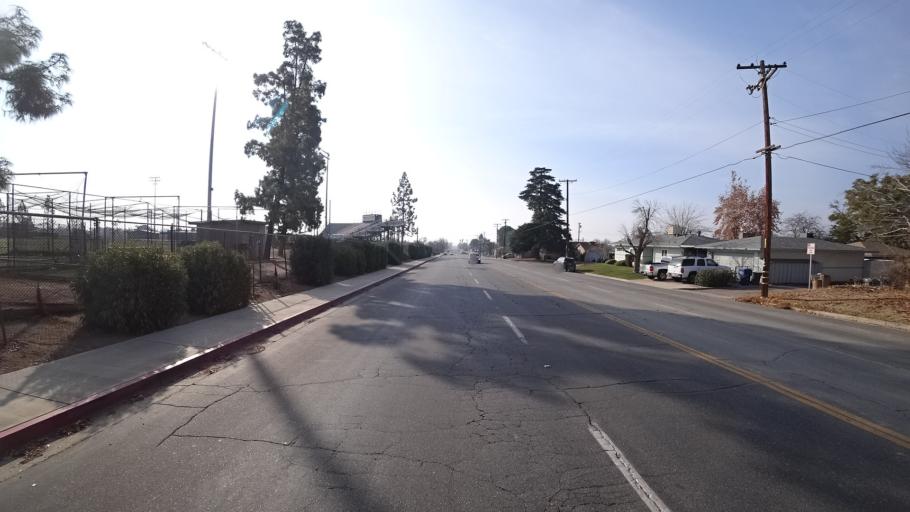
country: US
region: California
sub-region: Kern County
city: Oildale
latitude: 35.4071
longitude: -118.9764
